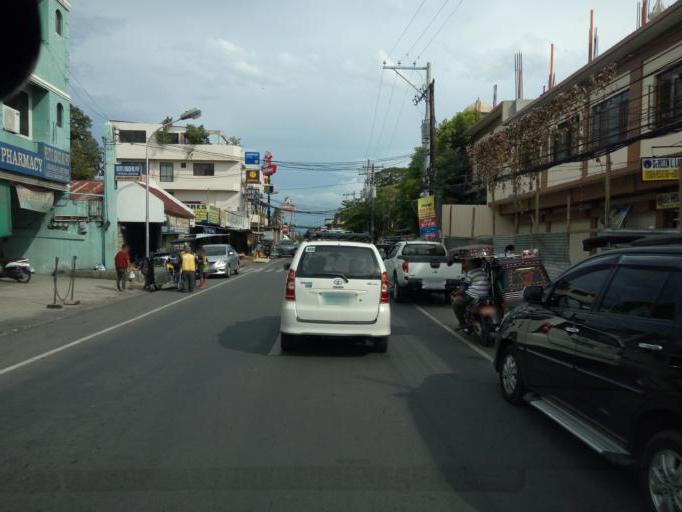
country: PH
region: Central Luzon
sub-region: Province of Nueva Ecija
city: Sibul
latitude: 15.7930
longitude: 120.9895
